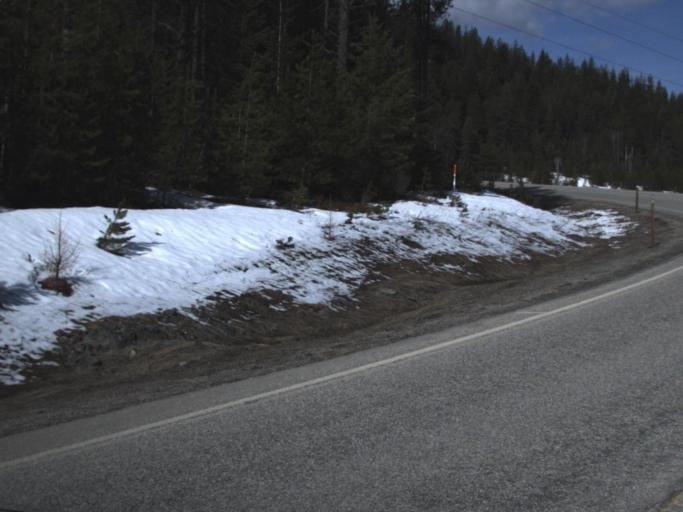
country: CA
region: British Columbia
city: Fruitvale
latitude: 48.6891
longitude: -117.4264
